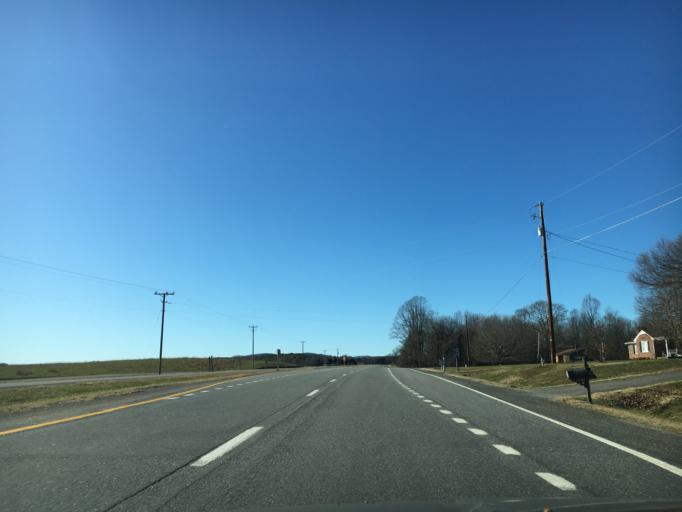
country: US
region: Virginia
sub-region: Patrick County
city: Patrick Springs
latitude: 36.6099
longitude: -80.1738
